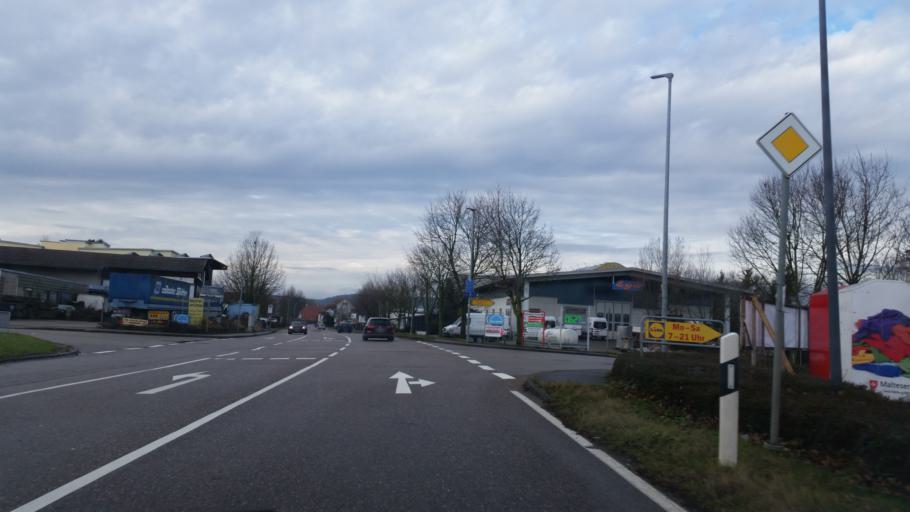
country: DE
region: Baden-Wuerttemberg
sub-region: Regierungsbezirk Stuttgart
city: Bretzfeld
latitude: 49.1809
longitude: 9.4093
